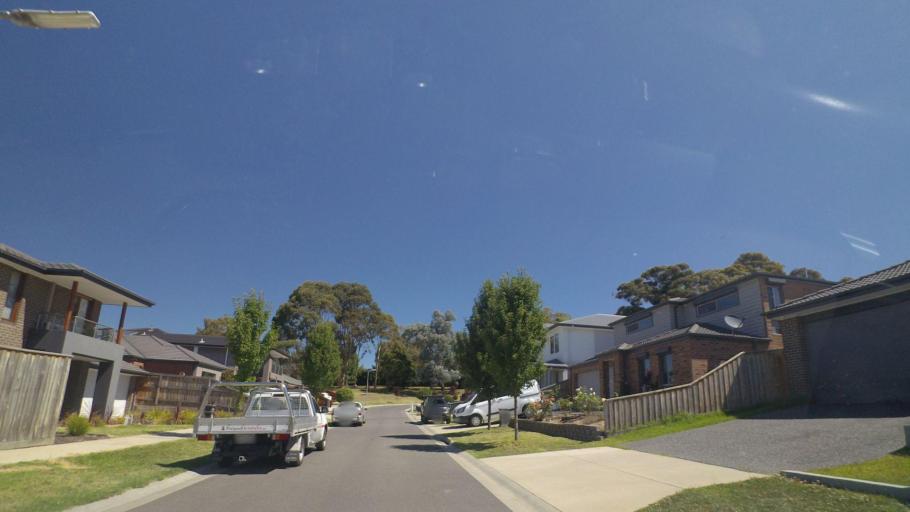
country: AU
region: Victoria
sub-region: Yarra Ranges
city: Chirnside Park
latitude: -37.7498
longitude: 145.3301
